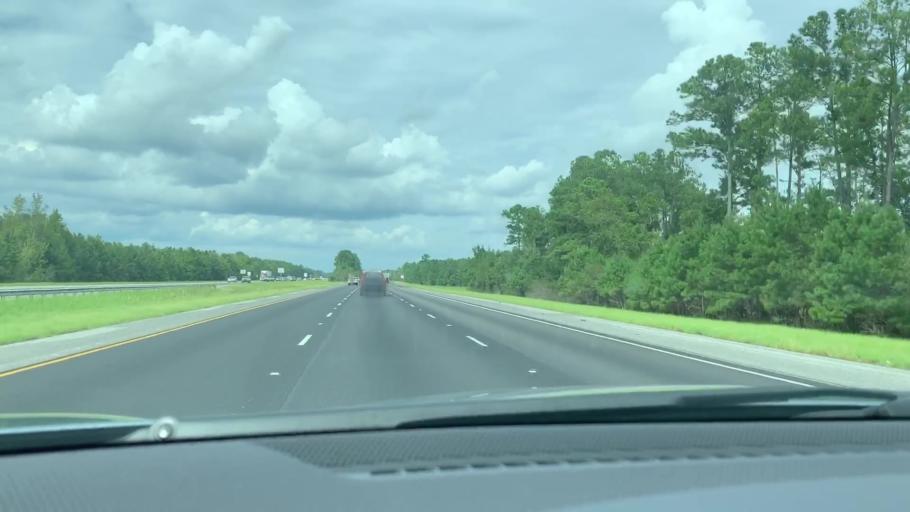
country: US
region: Georgia
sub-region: Liberty County
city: Midway
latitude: 31.7412
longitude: -81.3858
